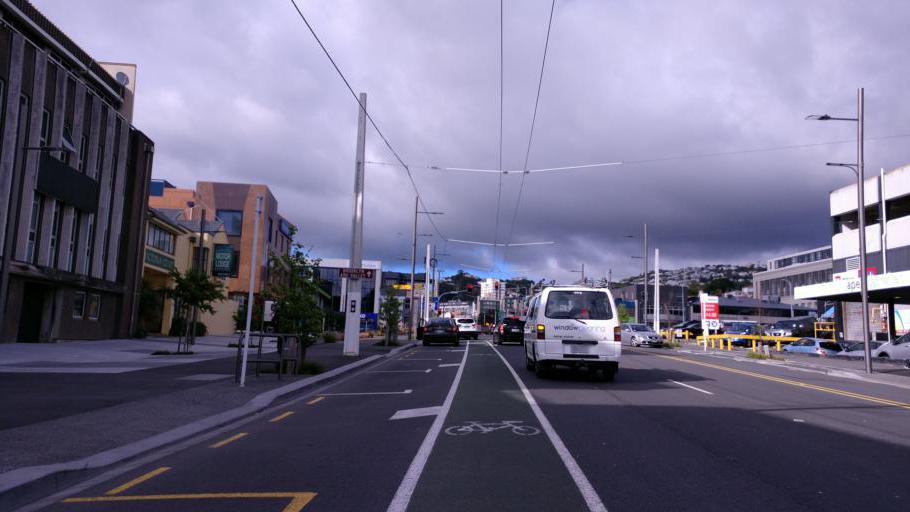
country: NZ
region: Wellington
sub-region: Wellington City
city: Wellington
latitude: -41.2932
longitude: 174.7737
